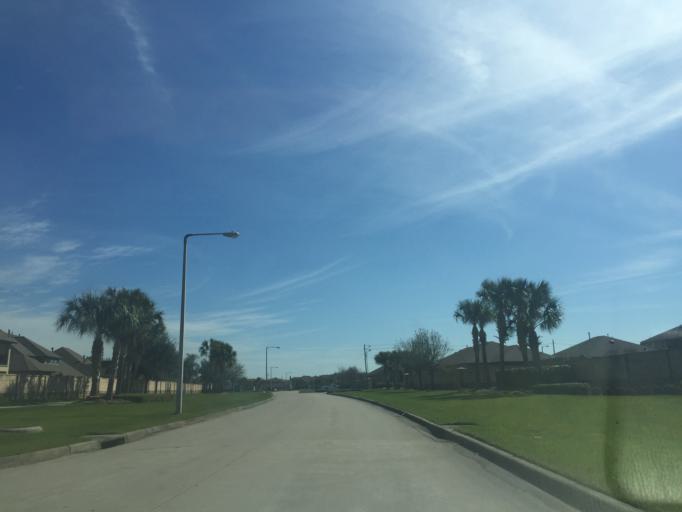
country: US
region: Texas
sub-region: Galveston County
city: Bacliff
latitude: 29.5116
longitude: -95.0179
